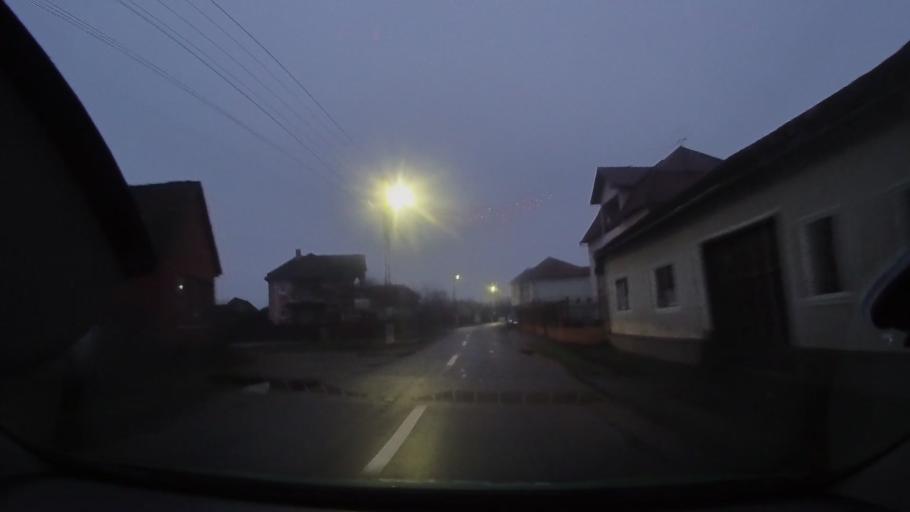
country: RO
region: Arad
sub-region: Comuna Archis
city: Archis
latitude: 46.4786
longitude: 22.0443
